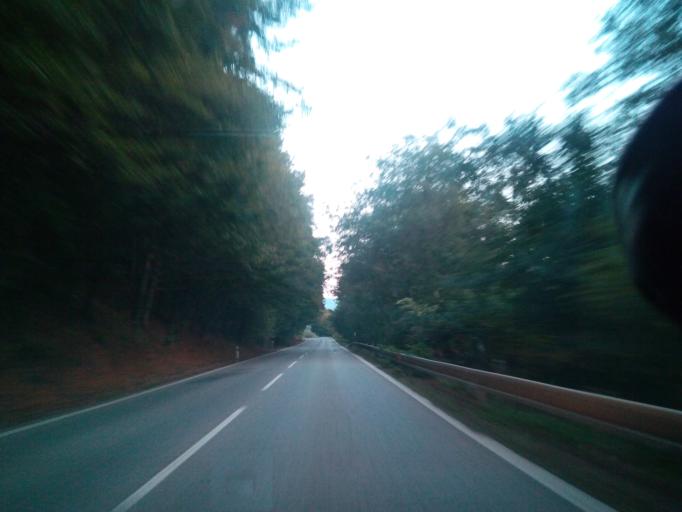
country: SK
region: Kosicky
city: Dobsina
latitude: 48.7961
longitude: 20.3941
